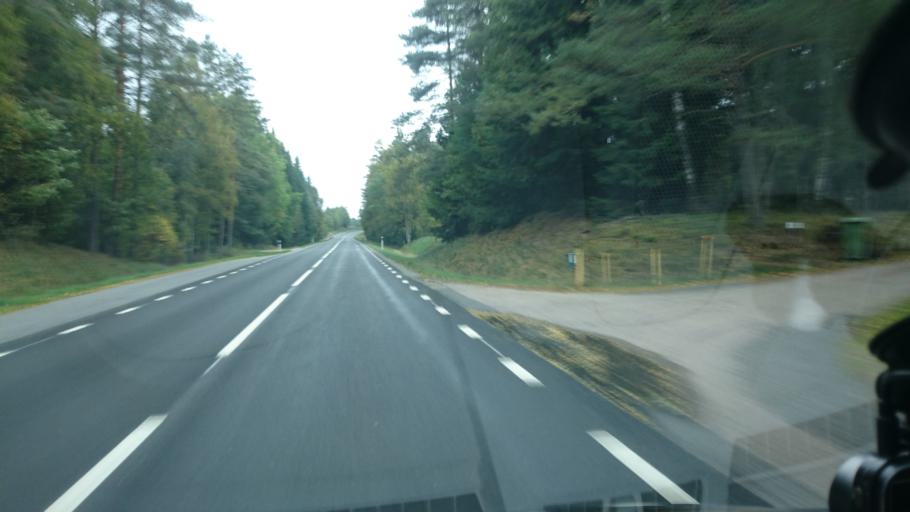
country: SE
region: Vaestra Goetaland
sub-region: Svenljunga Kommun
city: Svenljunga
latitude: 57.5418
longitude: 13.1215
